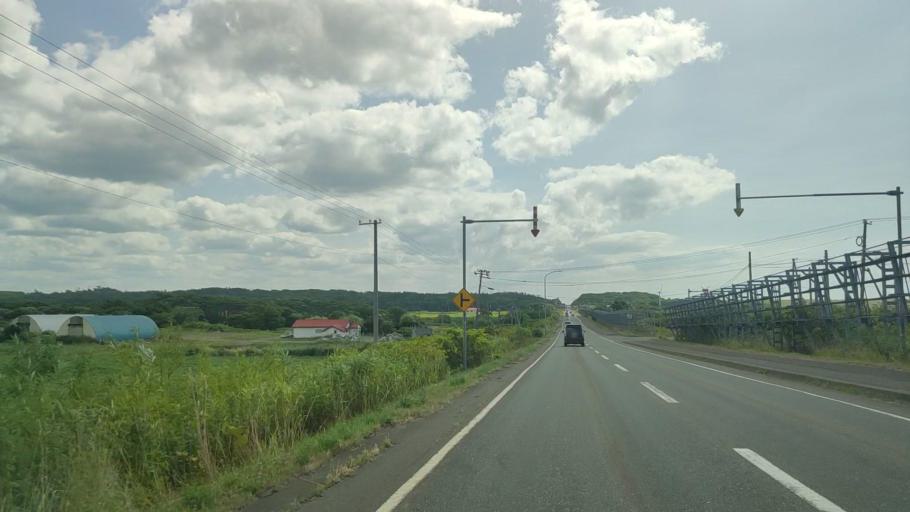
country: JP
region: Hokkaido
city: Makubetsu
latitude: 44.7760
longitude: 141.7917
